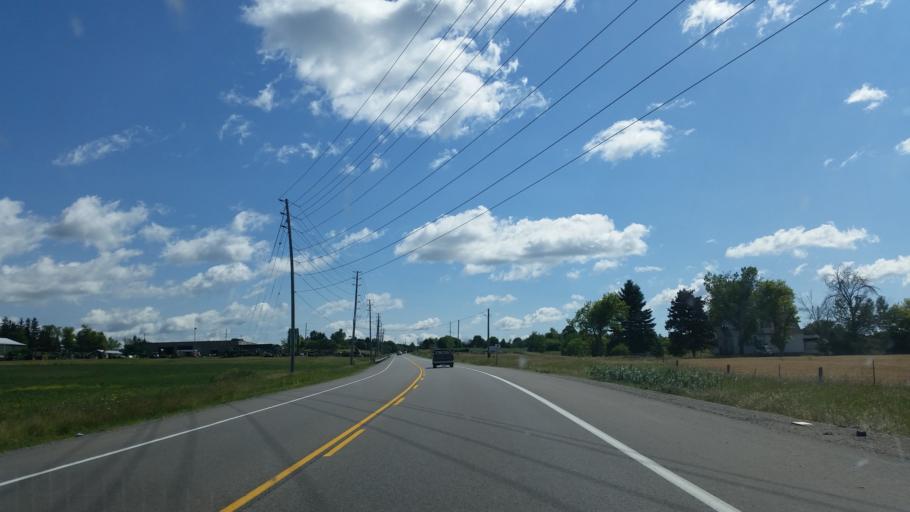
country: CA
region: Ontario
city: Vaughan
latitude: 43.8948
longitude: -79.6807
